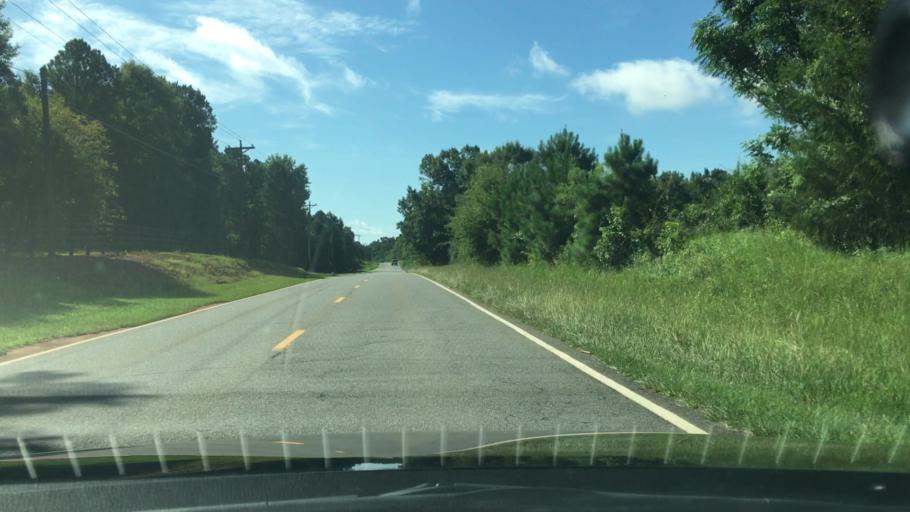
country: US
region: Georgia
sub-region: Putnam County
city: Jefferson
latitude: 33.4486
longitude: -83.2963
